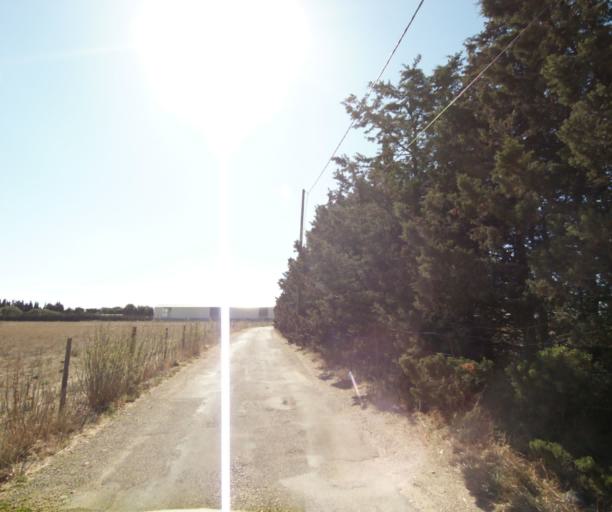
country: FR
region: Languedoc-Roussillon
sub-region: Departement du Gard
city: Rodilhan
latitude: 43.8180
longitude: 4.4430
